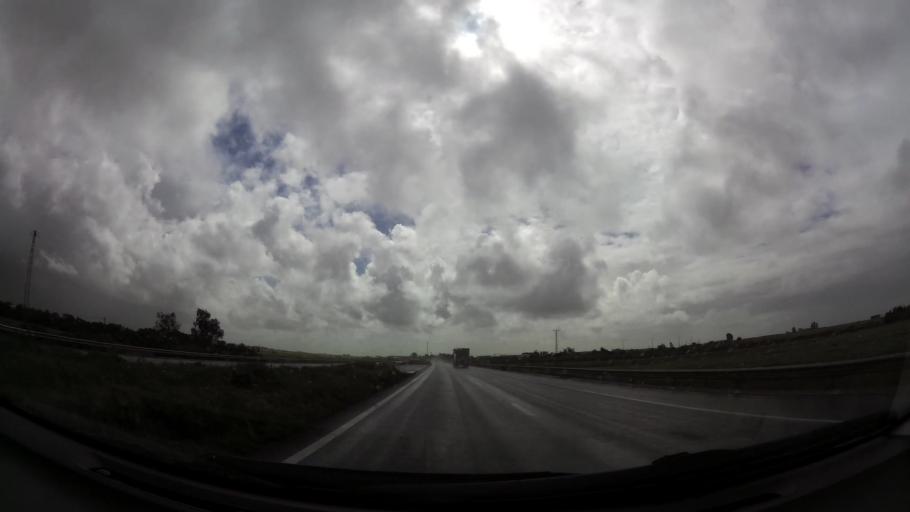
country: MA
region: Grand Casablanca
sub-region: Nouaceur
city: Dar Bouazza
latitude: 33.3875
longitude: -7.8837
